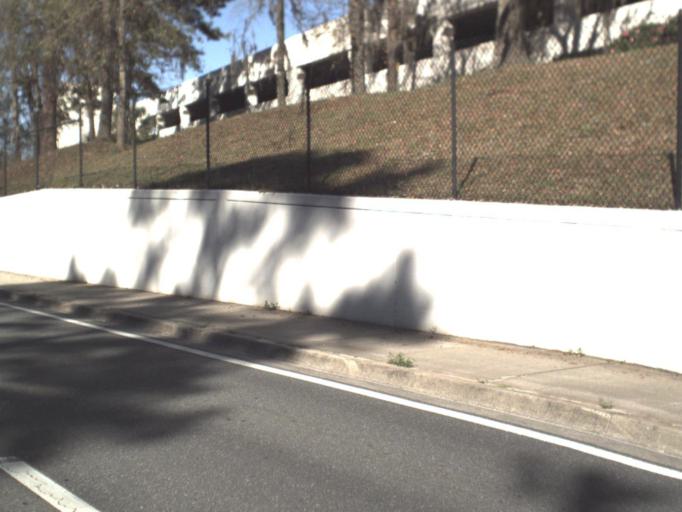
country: US
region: Florida
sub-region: Leon County
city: Tallahassee
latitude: 30.4577
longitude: -84.2628
